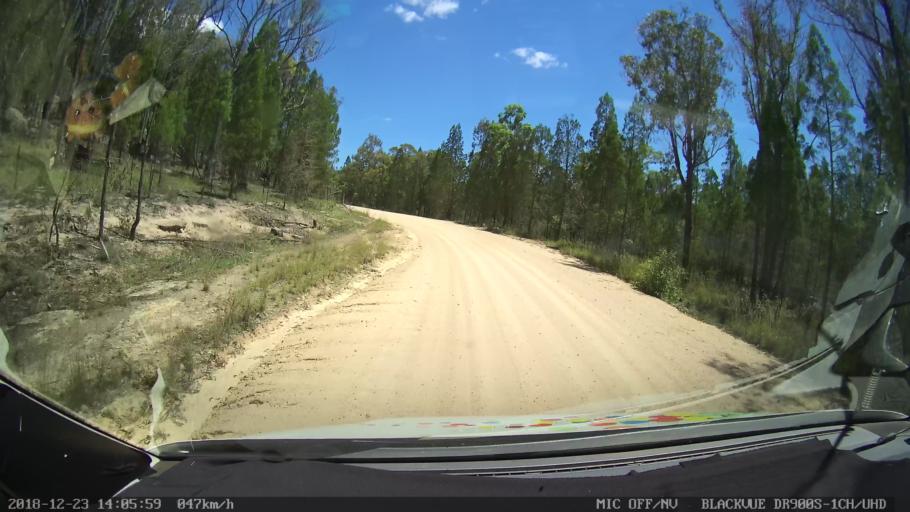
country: AU
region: New South Wales
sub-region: Tamworth Municipality
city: Manilla
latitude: -30.6275
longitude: 151.0773
